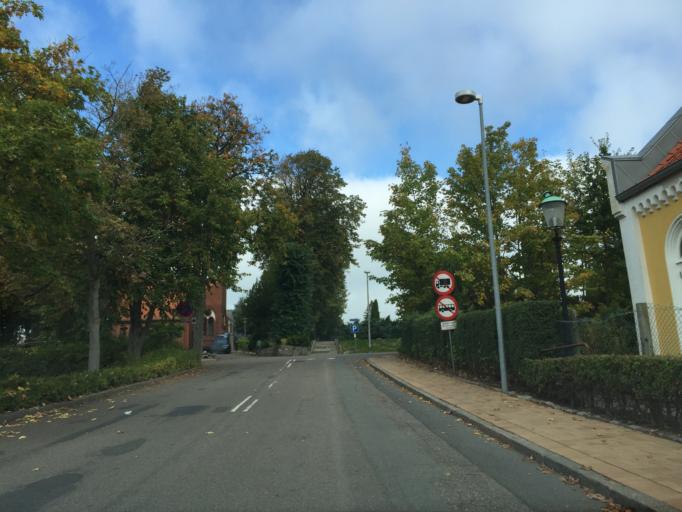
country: DK
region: South Denmark
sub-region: Sonderborg Kommune
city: Sonderborg
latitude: 54.9118
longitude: 9.7881
